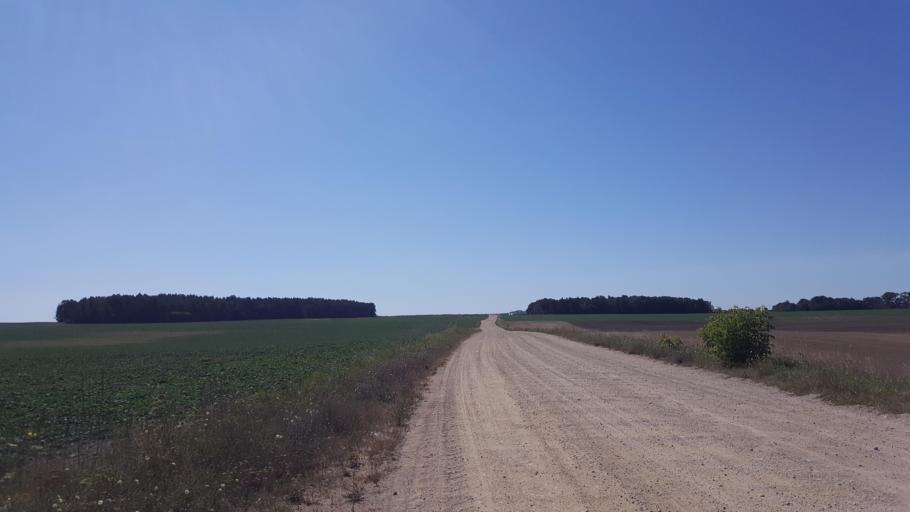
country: PL
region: Lublin Voivodeship
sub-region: Powiat bialski
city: Terespol
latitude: 52.2260
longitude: 23.5244
